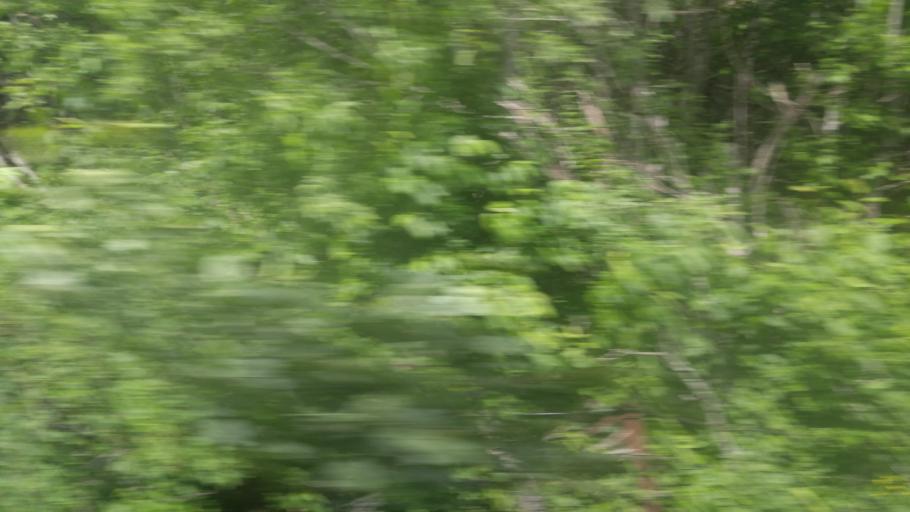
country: NO
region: Sor-Trondelag
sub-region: Klaebu
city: Klaebu
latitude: 62.9502
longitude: 10.6839
